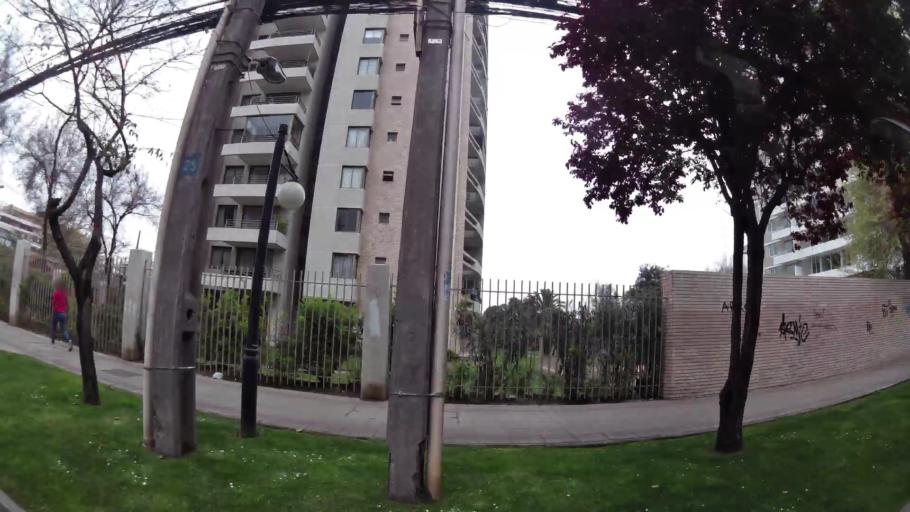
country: CL
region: Santiago Metropolitan
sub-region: Provincia de Santiago
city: Villa Presidente Frei, Nunoa, Santiago, Chile
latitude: -33.4614
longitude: -70.6002
